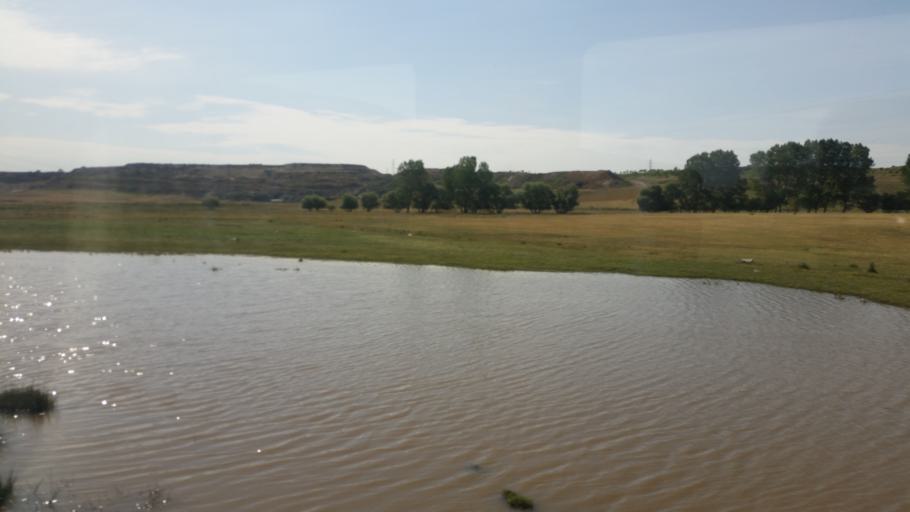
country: TR
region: Tekirdag
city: Corlu
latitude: 41.1855
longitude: 27.7972
